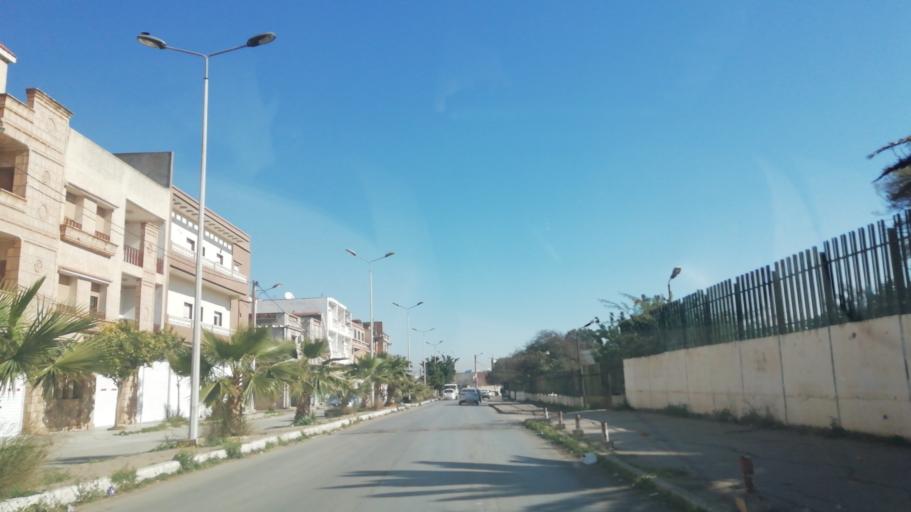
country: DZ
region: Oran
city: Oran
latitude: 35.6713
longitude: -0.6359
